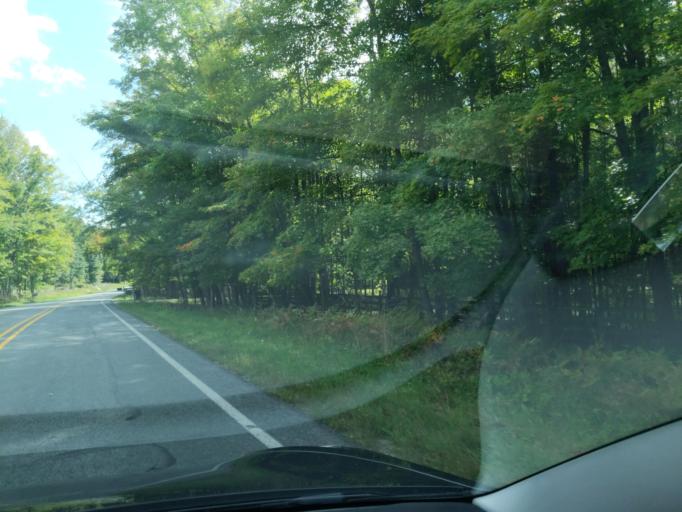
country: US
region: Michigan
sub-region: Antrim County
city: Bellaire
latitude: 45.0330
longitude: -85.2960
